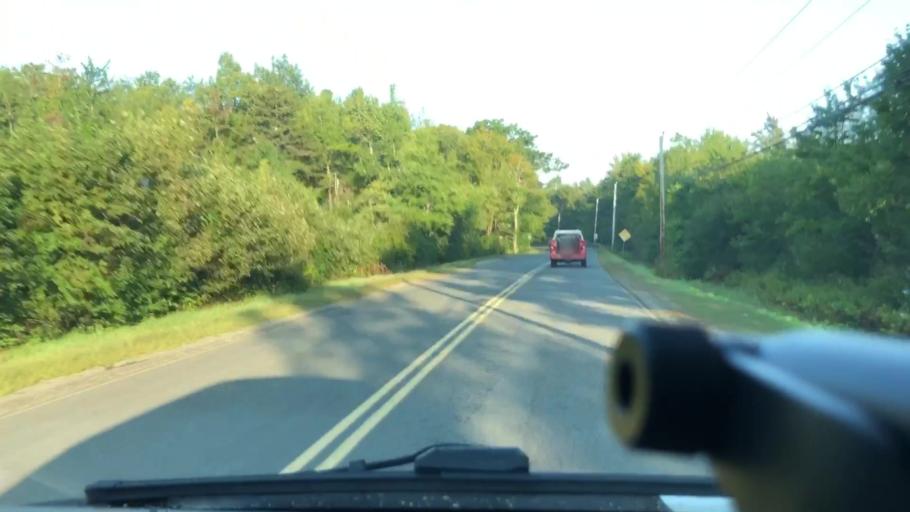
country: US
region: Massachusetts
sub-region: Franklin County
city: Ashfield
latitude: 42.5111
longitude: -72.8190
